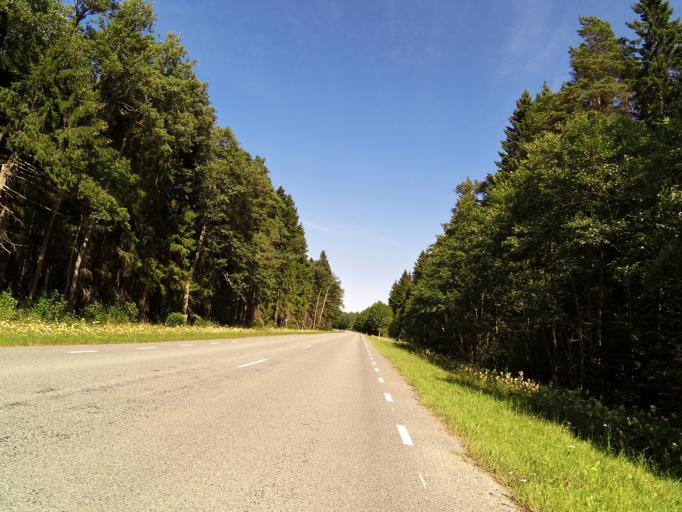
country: EE
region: Hiiumaa
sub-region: Kaerdla linn
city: Kardla
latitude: 58.9374
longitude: 22.4060
